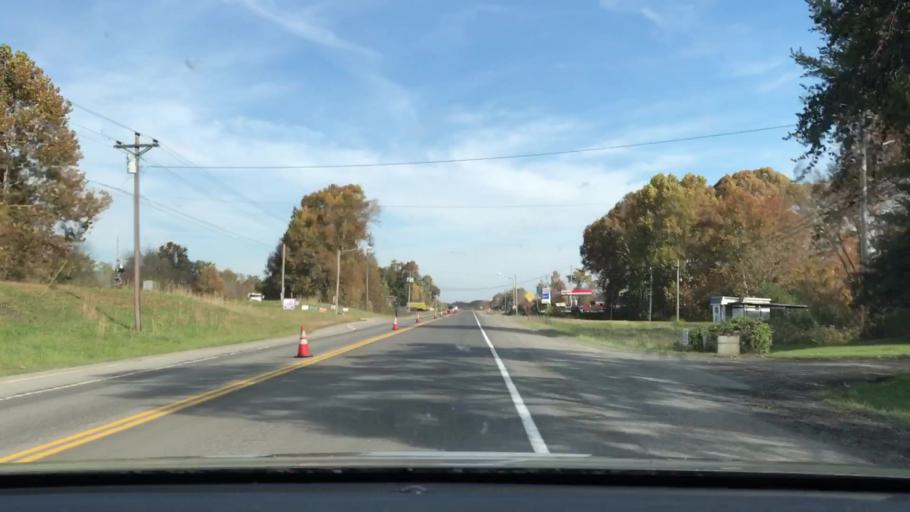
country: US
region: Tennessee
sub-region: Scott County
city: Oneida
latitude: 36.5562
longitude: -84.4509
